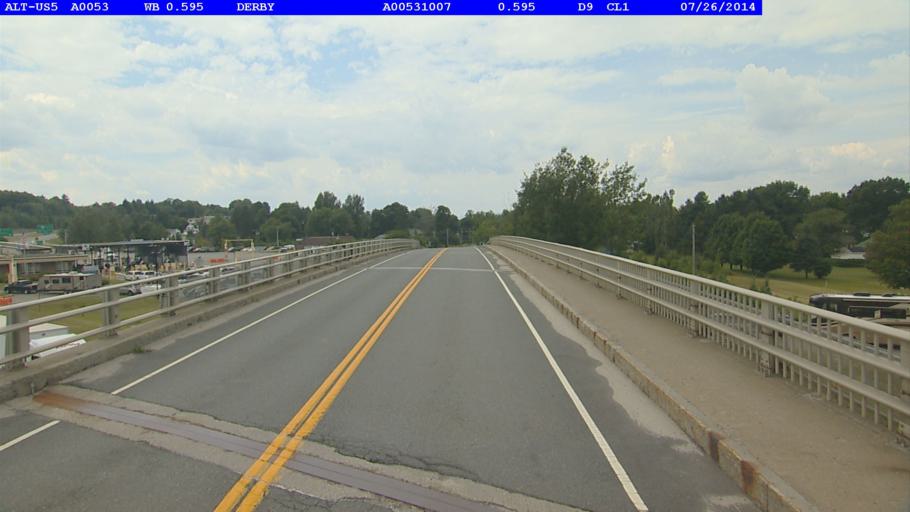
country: US
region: Vermont
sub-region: Orleans County
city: Newport
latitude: 45.0053
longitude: -72.0878
